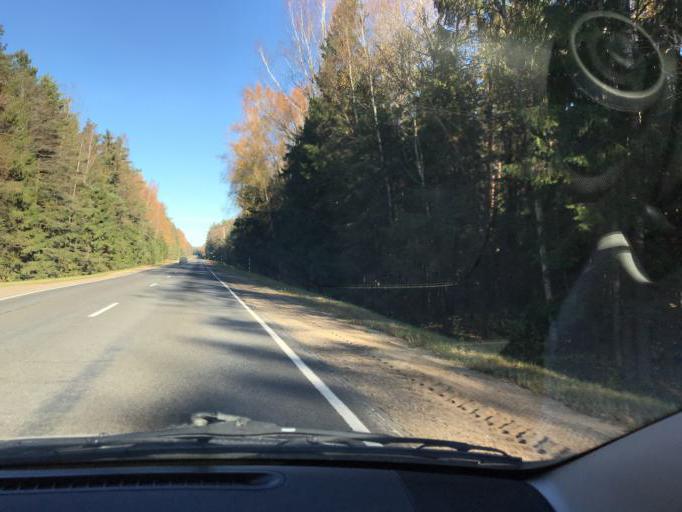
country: BY
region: Vitebsk
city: Polatsk
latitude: 55.3683
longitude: 28.8092
